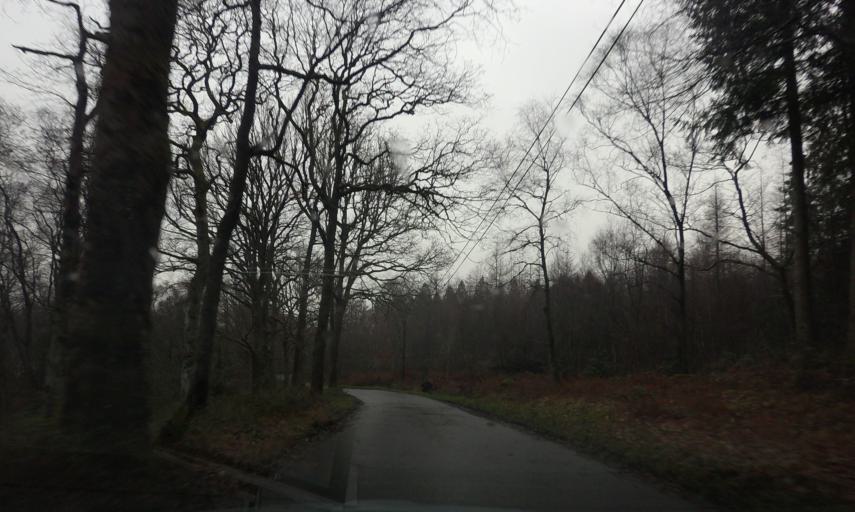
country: GB
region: Scotland
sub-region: West Dunbartonshire
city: Balloch
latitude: 56.1258
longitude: -4.6035
